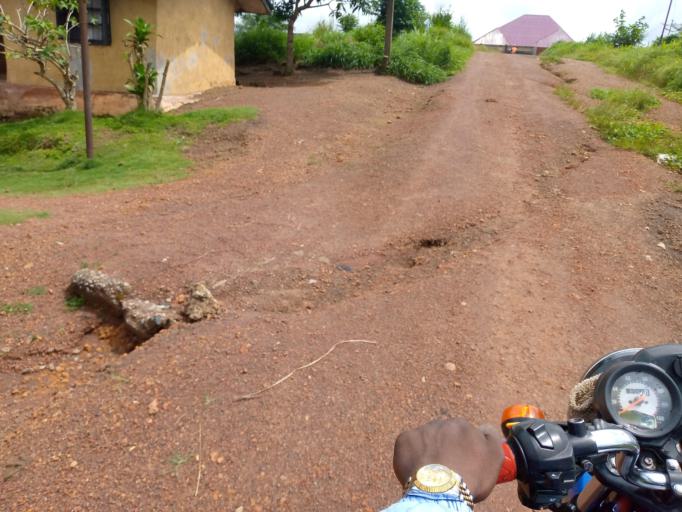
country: SL
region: Eastern Province
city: Kenema
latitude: 7.8782
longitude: -11.1666
